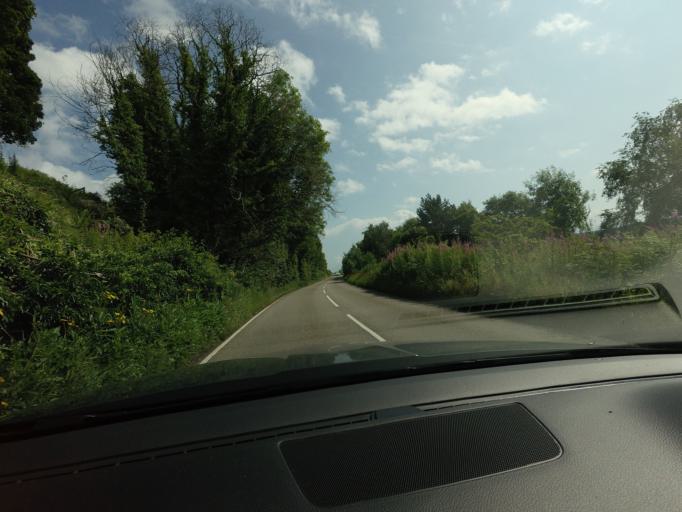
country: GB
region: Scotland
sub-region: Highland
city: Dingwall
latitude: 57.6113
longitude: -4.4063
